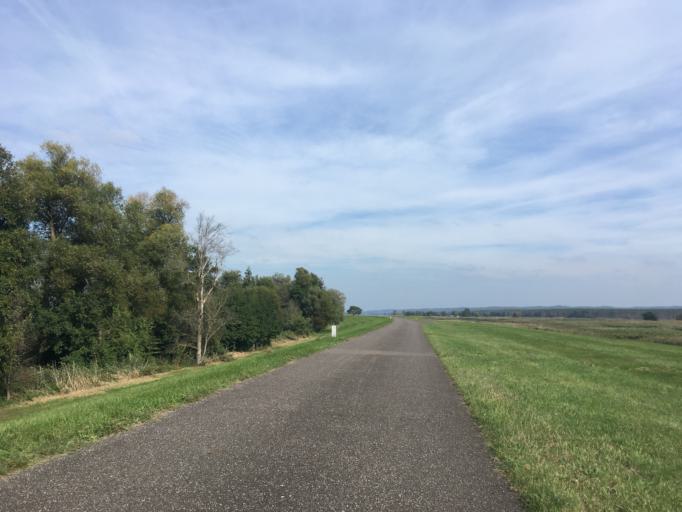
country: DE
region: Brandenburg
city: Schoneberg
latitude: 52.9687
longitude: 14.1514
